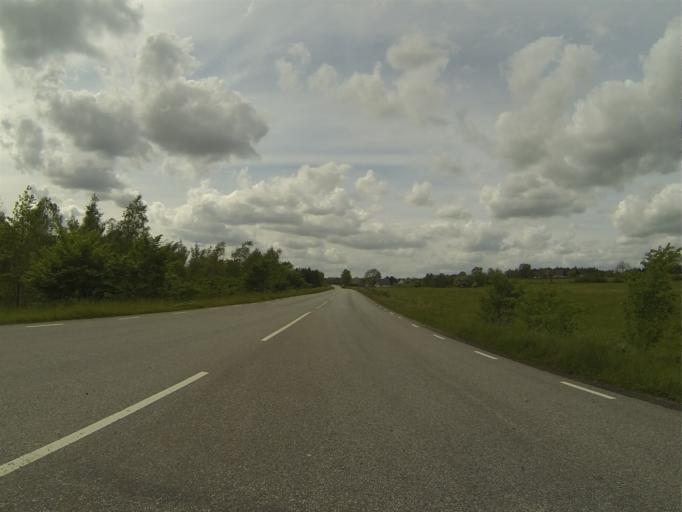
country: SE
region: Skane
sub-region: Sjobo Kommun
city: Sjoebo
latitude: 55.6535
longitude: 13.6994
